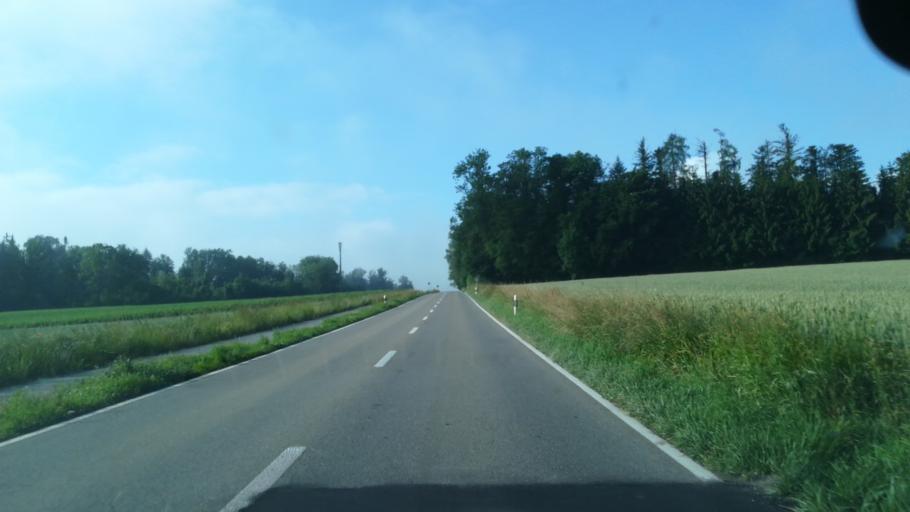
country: CH
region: Thurgau
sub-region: Kreuzlingen District
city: Kreuzlingen
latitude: 47.6270
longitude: 9.1674
